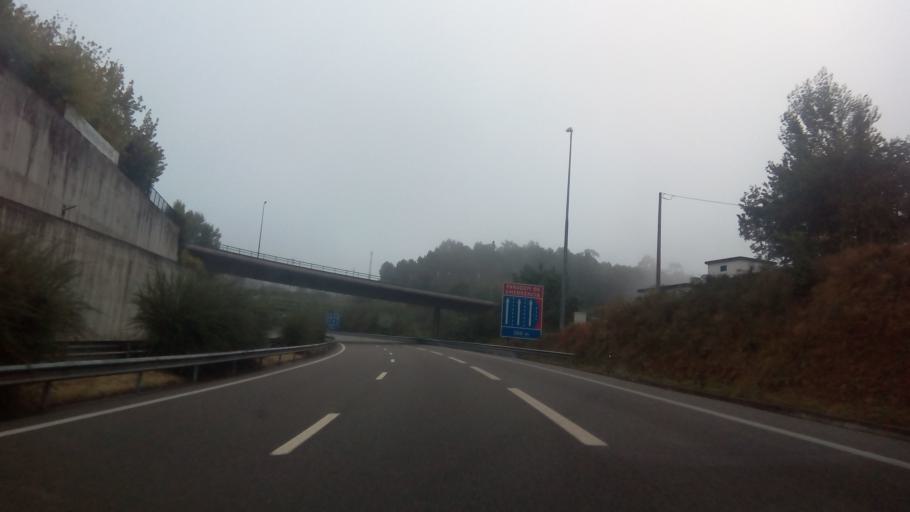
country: PT
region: Porto
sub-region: Marco de Canaveses
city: Marco de Canavezes
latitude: 41.2191
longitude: -8.1519
